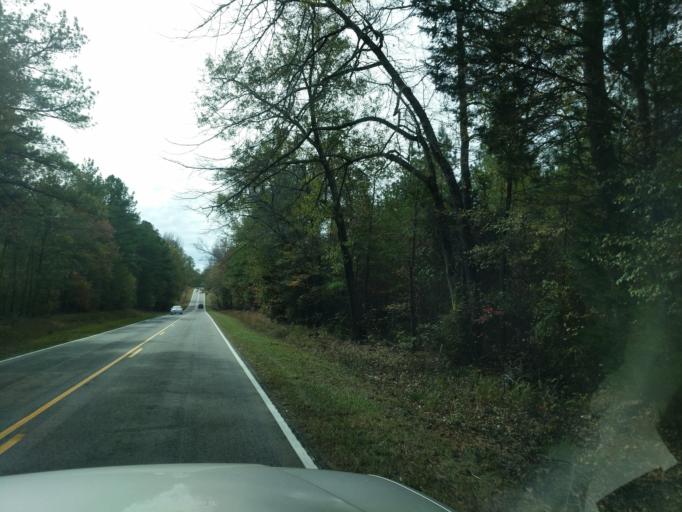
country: US
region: South Carolina
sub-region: Greenwood County
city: Ninety Six
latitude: 34.2442
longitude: -81.8700
